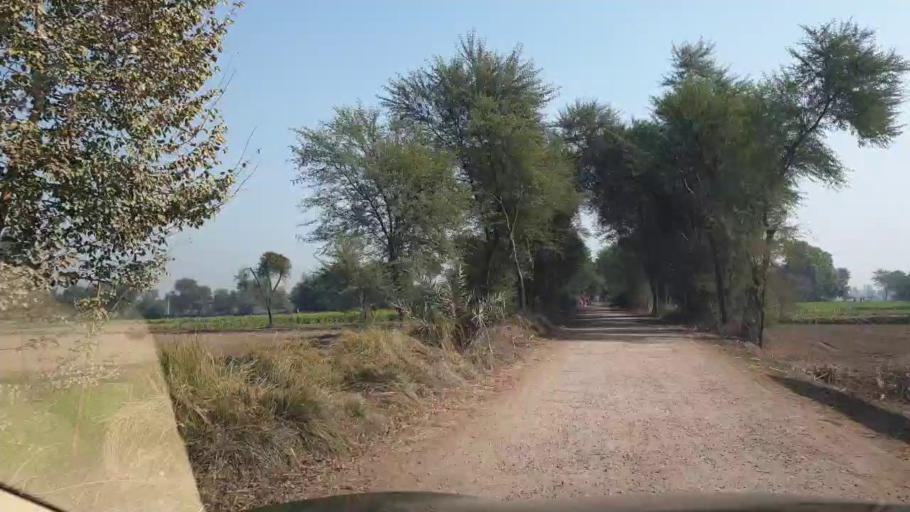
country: PK
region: Sindh
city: Ubauro
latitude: 28.1102
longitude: 69.7718
